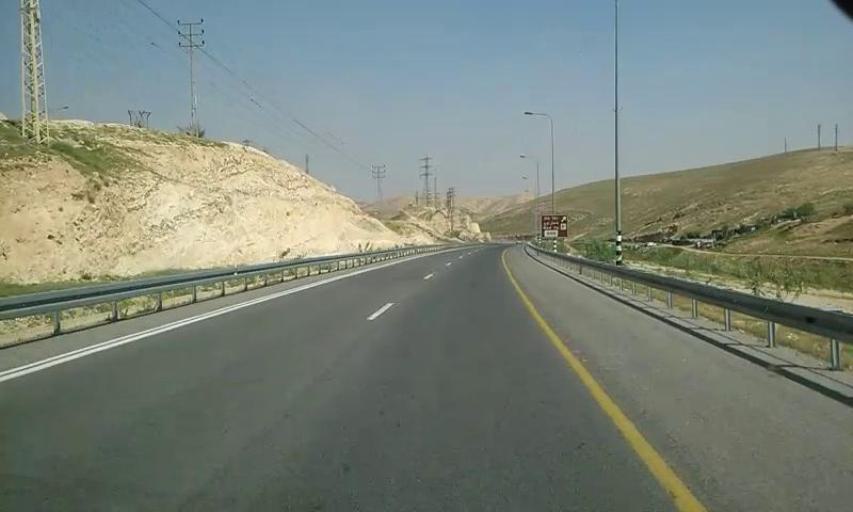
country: PS
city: Az Za`ayyim
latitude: 31.8083
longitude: 35.3333
